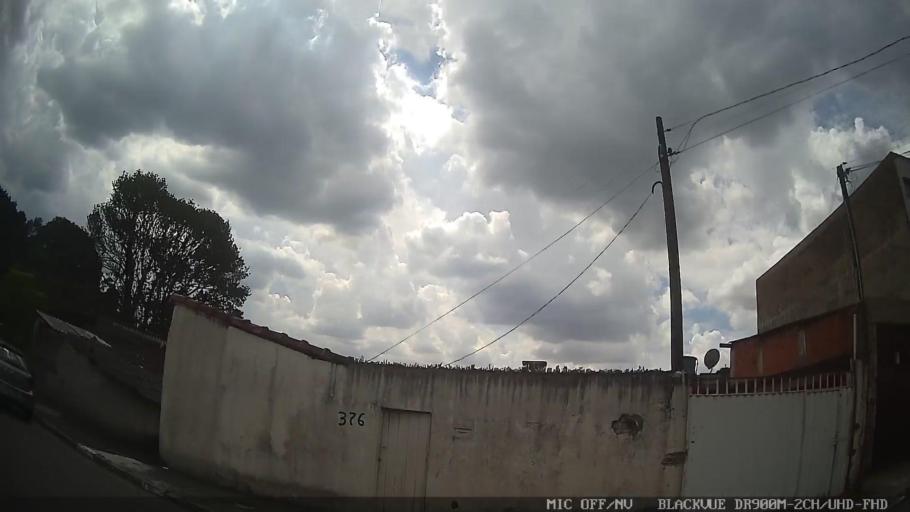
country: BR
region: Sao Paulo
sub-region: Ribeirao Pires
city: Ribeirao Pires
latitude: -23.7235
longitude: -46.4255
